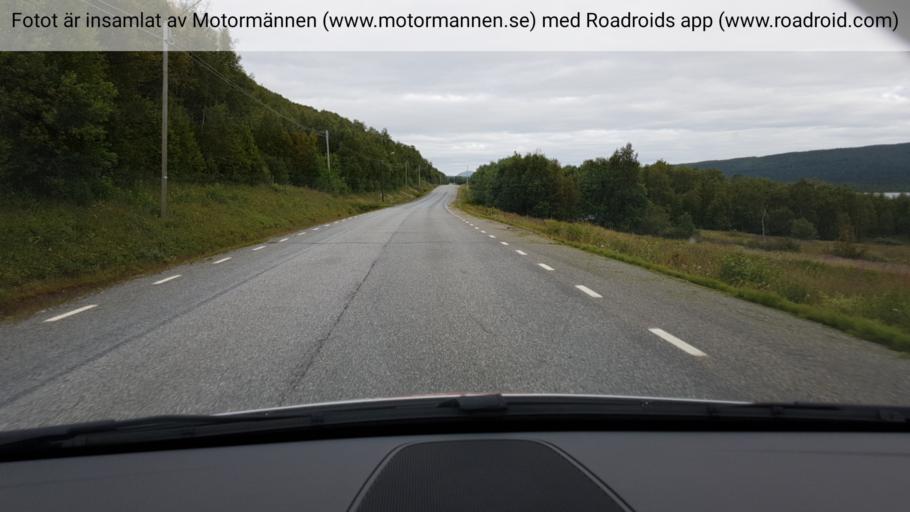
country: NO
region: Nordland
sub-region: Hattfjelldal
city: Hattfjelldal
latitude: 65.0574
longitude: 14.9149
